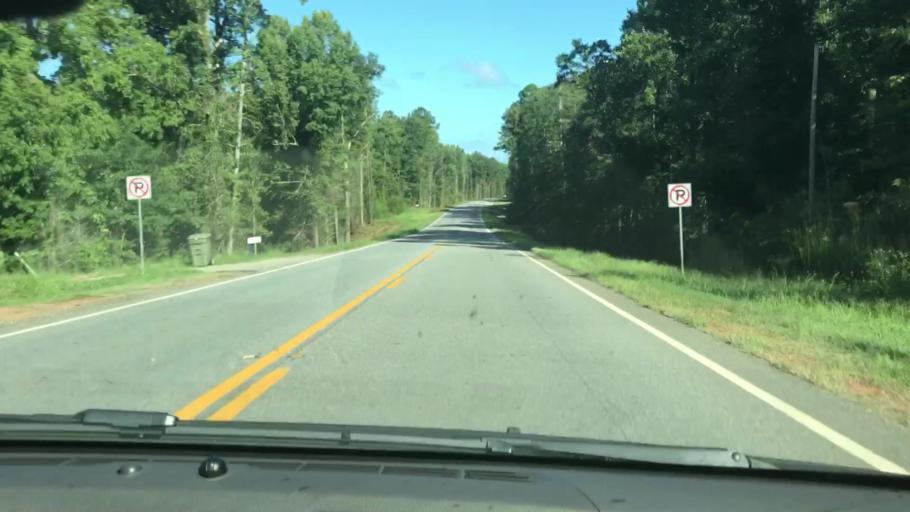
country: US
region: Georgia
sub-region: Quitman County
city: Georgetown
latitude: 31.8692
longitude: -85.0766
